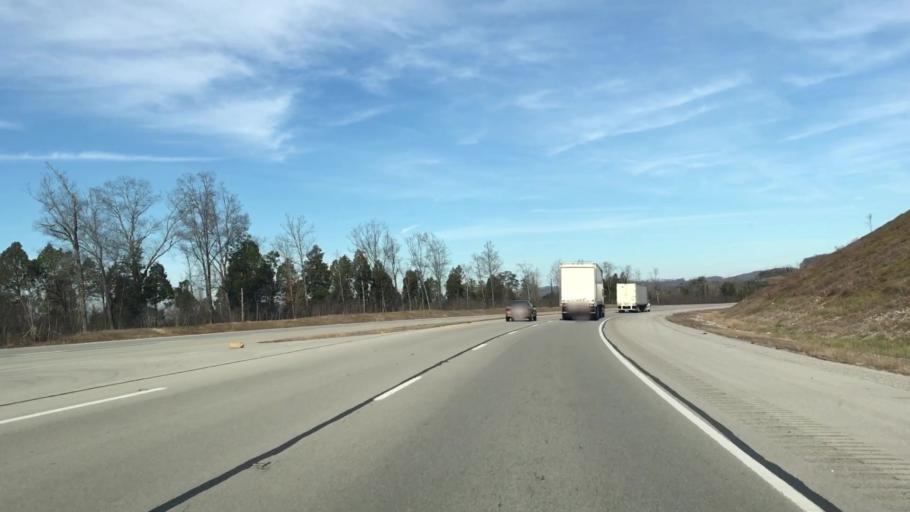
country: US
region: Kentucky
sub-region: Pulaski County
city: Somerset
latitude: 37.0145
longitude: -84.6004
